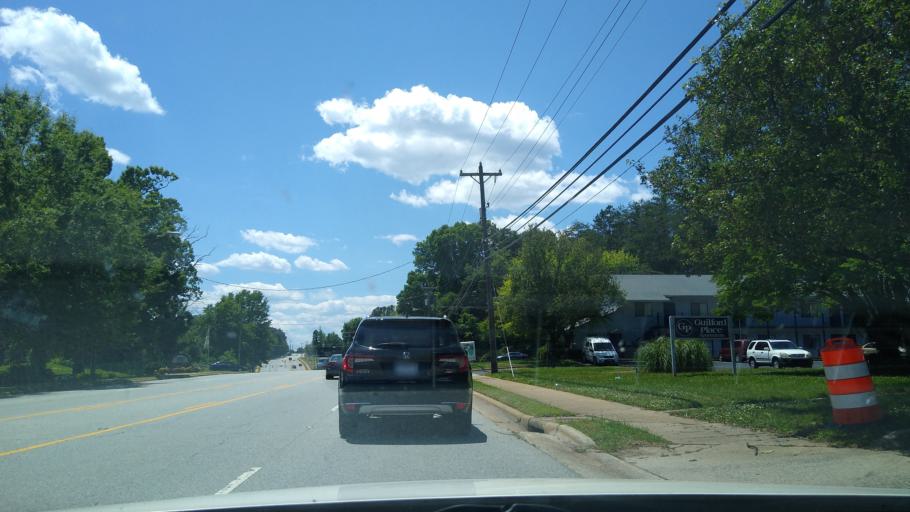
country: US
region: North Carolina
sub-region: Guilford County
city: Jamestown
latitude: 36.0694
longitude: -79.9019
